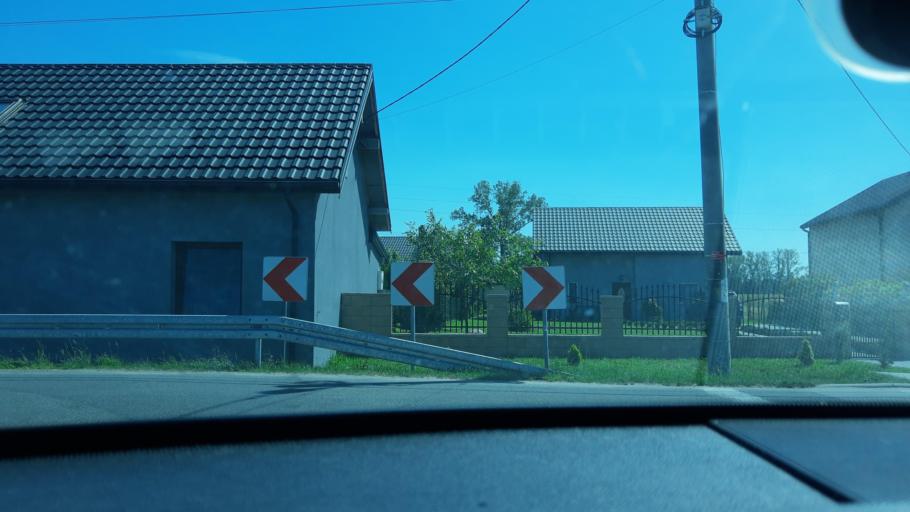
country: PL
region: Lodz Voivodeship
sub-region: Powiat zdunskowolski
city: Zdunska Wola
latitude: 51.6178
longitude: 18.9776
